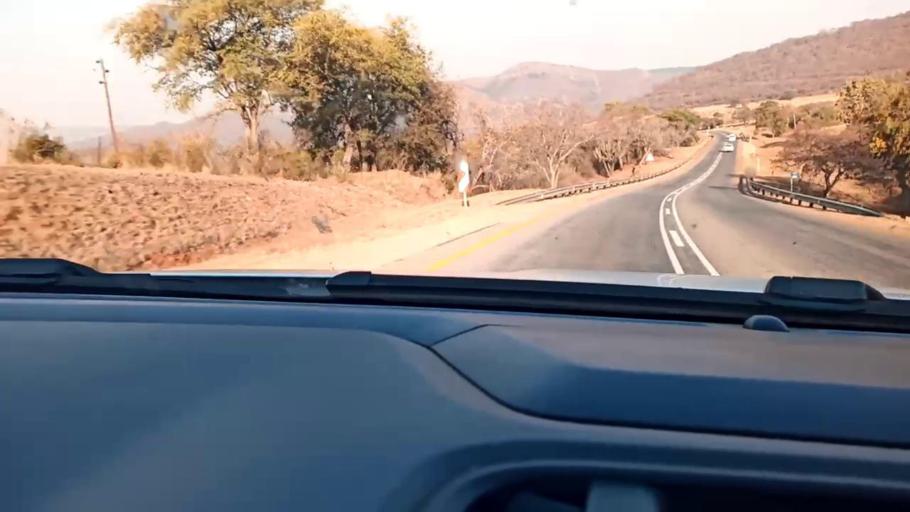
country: ZA
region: Limpopo
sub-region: Mopani District Municipality
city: Duiwelskloof
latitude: -23.6412
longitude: 30.1585
